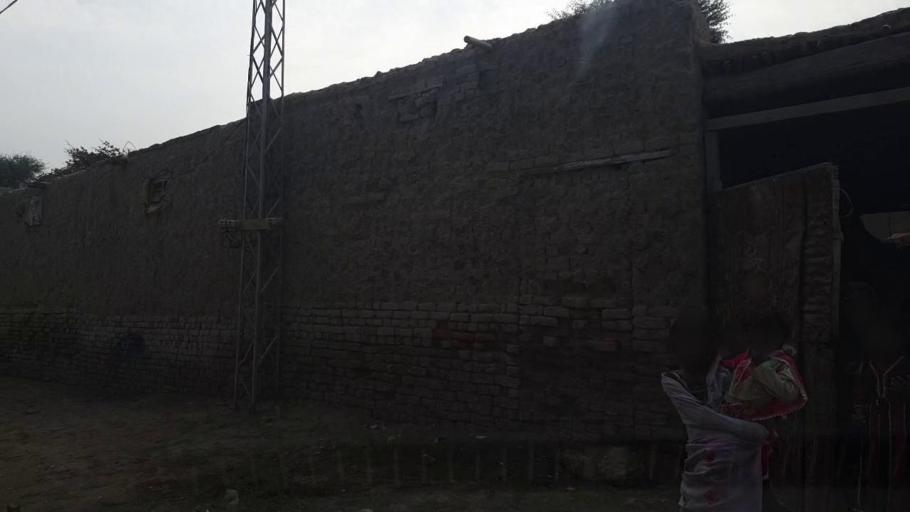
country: PK
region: Sindh
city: Sann
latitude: 25.9871
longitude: 68.1860
